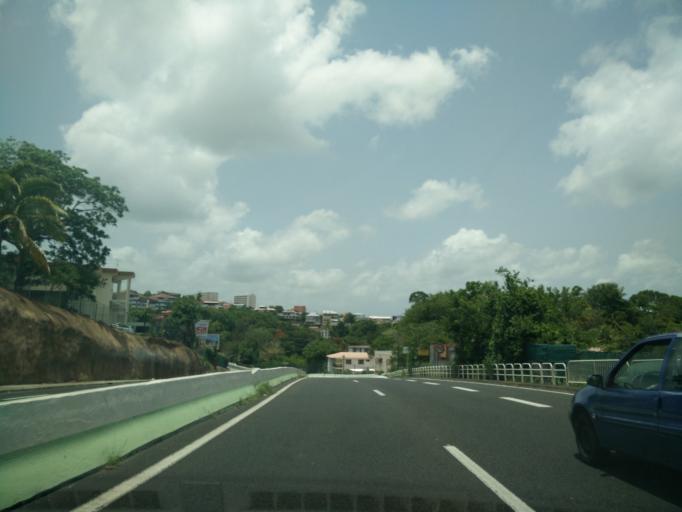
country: MQ
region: Martinique
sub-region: Martinique
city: Fort-de-France
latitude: 14.6157
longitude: -61.0987
